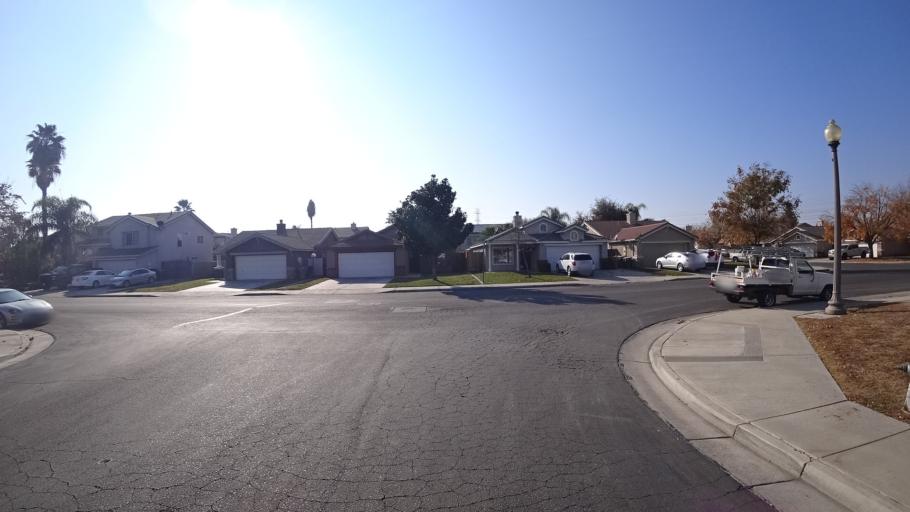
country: US
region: California
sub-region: Kern County
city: Greenacres
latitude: 35.3214
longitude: -119.0940
